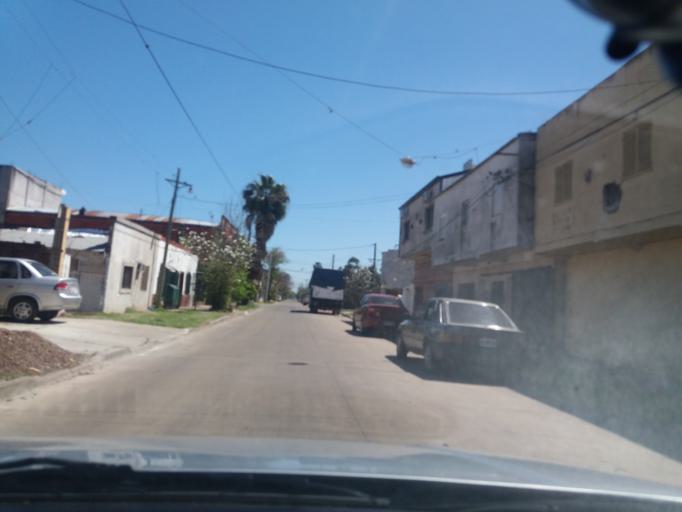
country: AR
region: Corrientes
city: Corrientes
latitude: -27.4898
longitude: -58.8334
